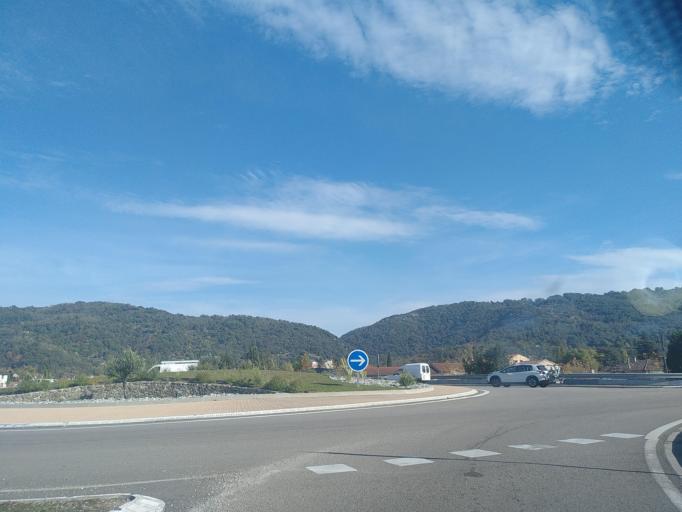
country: FR
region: Rhone-Alpes
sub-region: Departement de la Drome
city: Saint-Vallier
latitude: 45.1728
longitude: 4.8138
